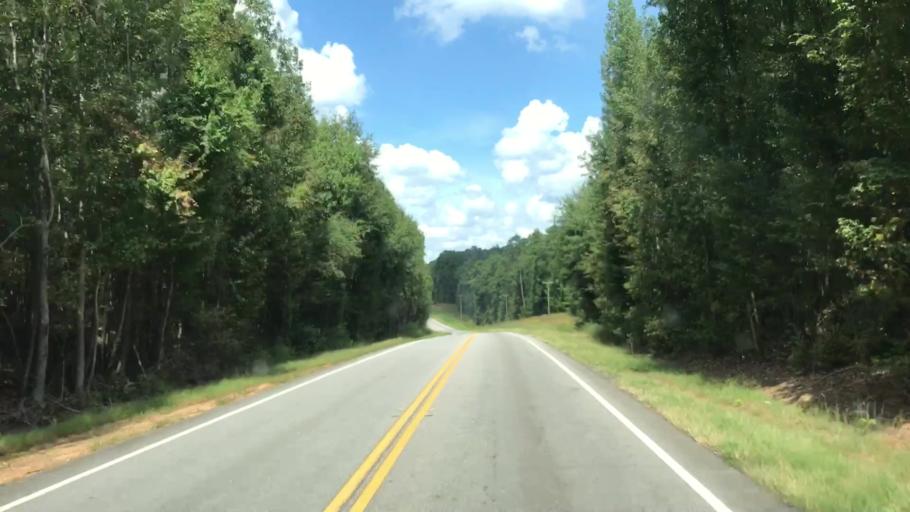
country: US
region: Georgia
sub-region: Greene County
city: Greensboro
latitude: 33.6524
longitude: -83.2362
